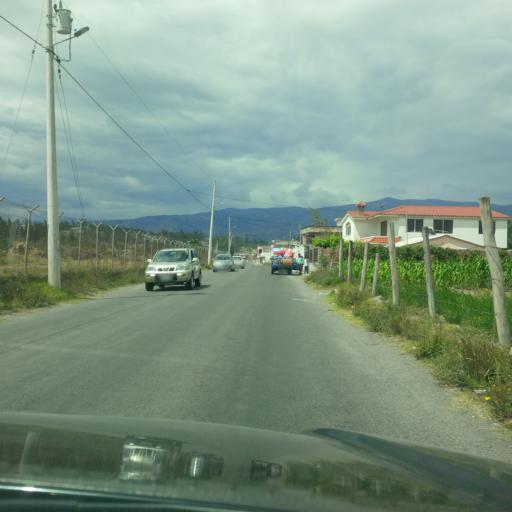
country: EC
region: Chimborazo
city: Riobamba
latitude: -1.6446
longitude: -78.6519
